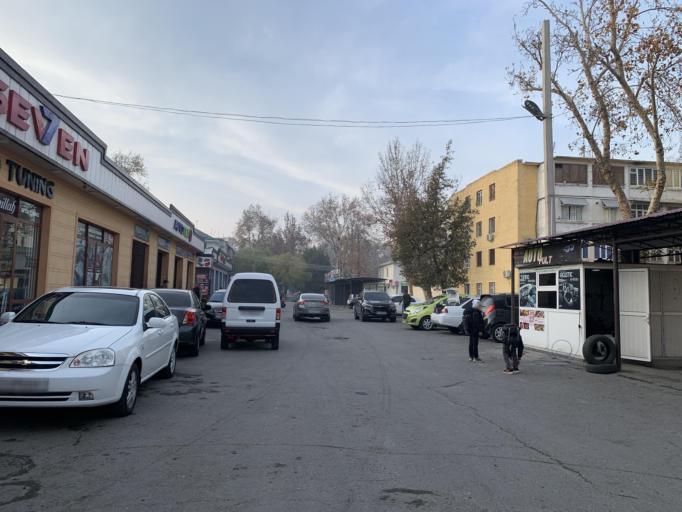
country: UZ
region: Fergana
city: Qo`qon
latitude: 40.5453
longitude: 70.9255
